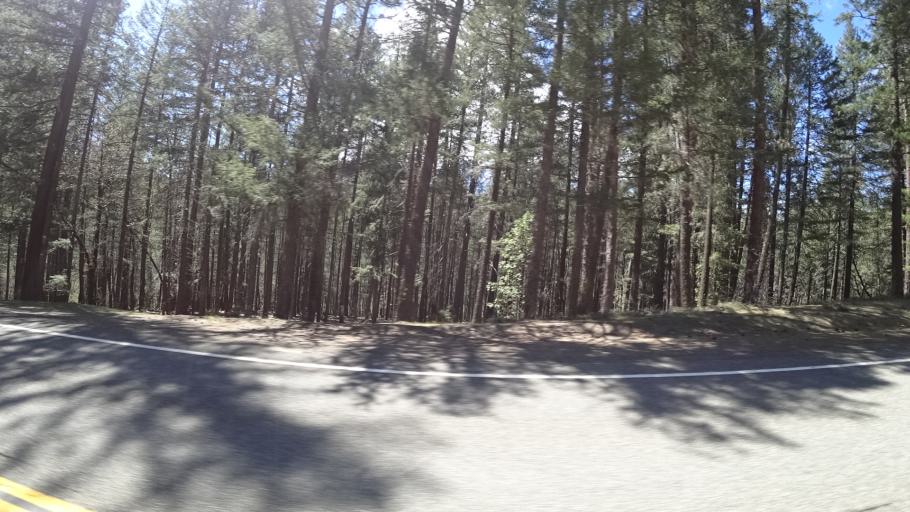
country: US
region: California
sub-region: Trinity County
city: Weaverville
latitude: 40.7839
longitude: -122.8929
